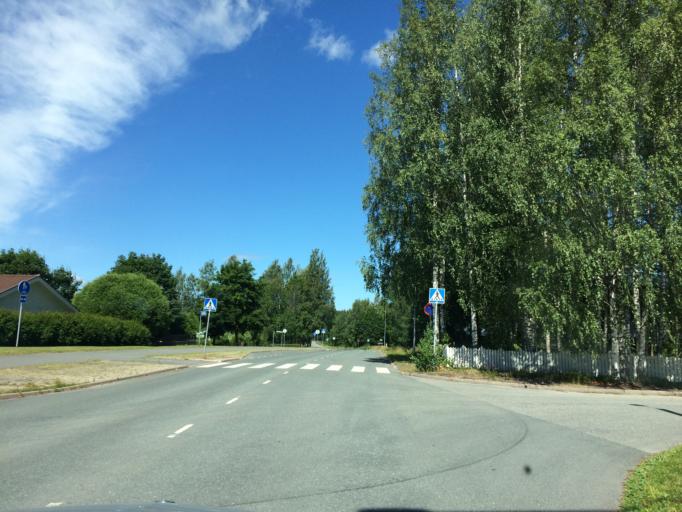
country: FI
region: Haeme
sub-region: Haemeenlinna
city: Haemeenlinna
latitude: 60.9663
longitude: 24.4726
